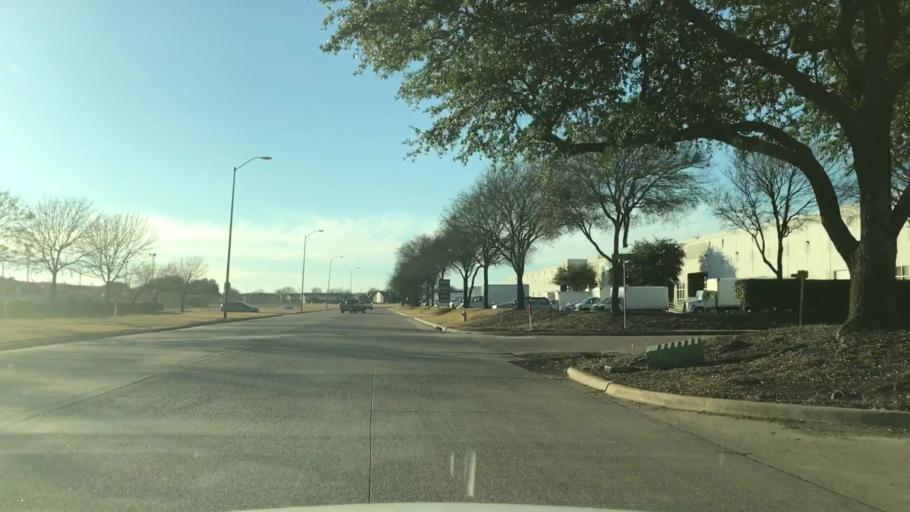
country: US
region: Texas
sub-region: Dallas County
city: Balch Springs
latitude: 32.7843
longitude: -96.6780
